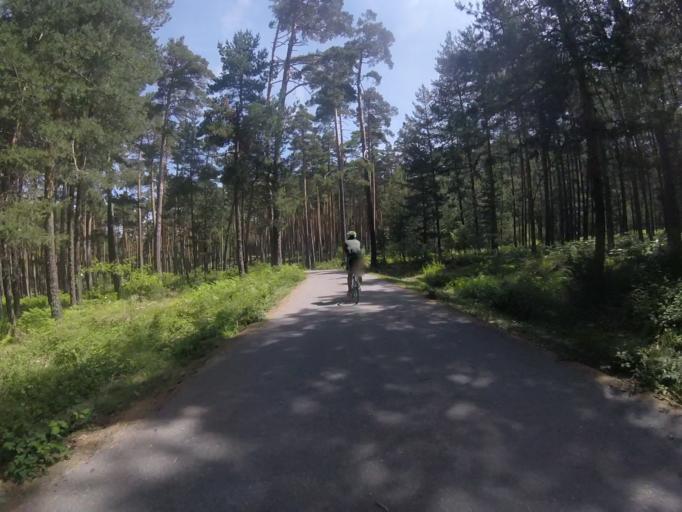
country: ES
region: Castille and Leon
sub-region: Provincia de Segovia
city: San Ildefonso
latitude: 40.8209
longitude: -4.0248
